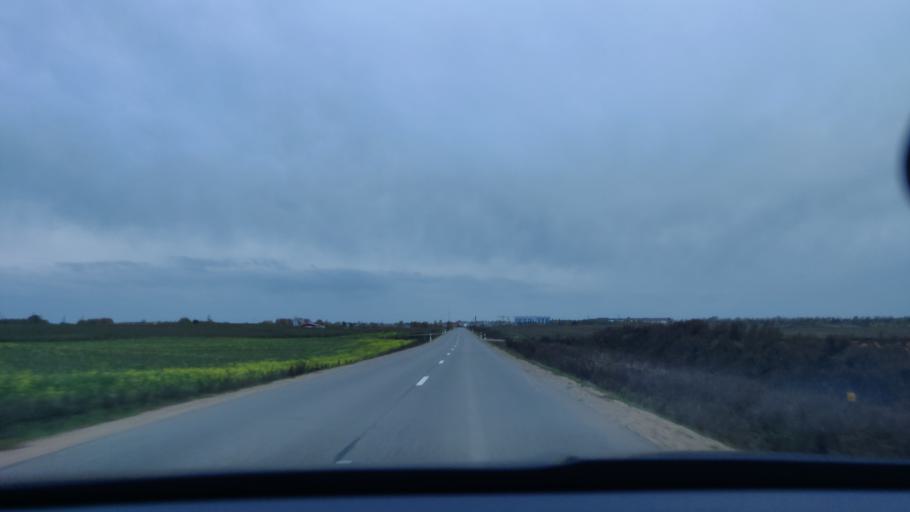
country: LT
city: Lentvaris
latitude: 54.6037
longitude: 25.0036
